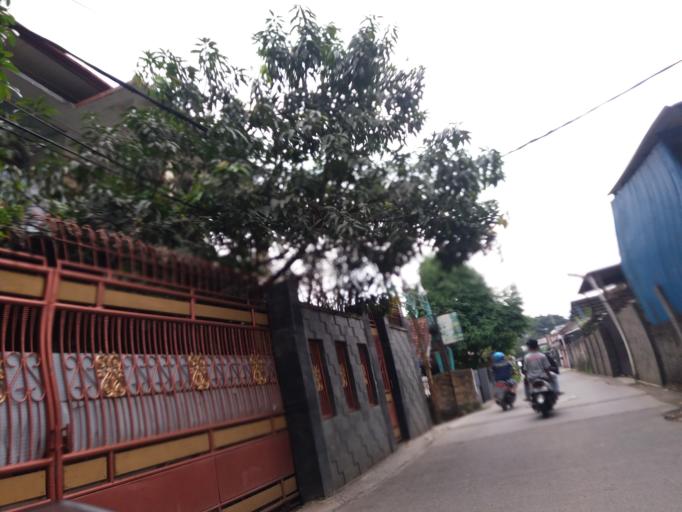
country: ID
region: West Java
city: Bandung
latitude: -6.9263
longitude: 107.6541
